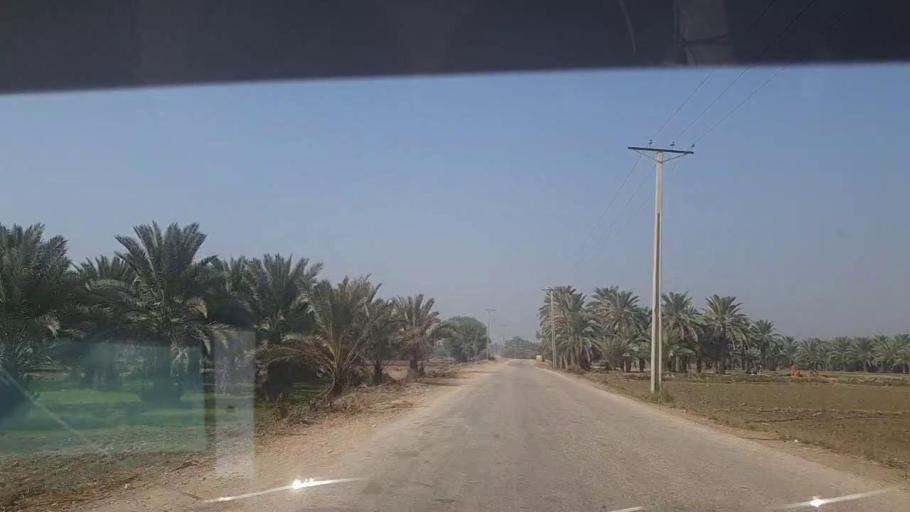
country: PK
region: Sindh
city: Kot Diji
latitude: 27.3726
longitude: 68.6985
